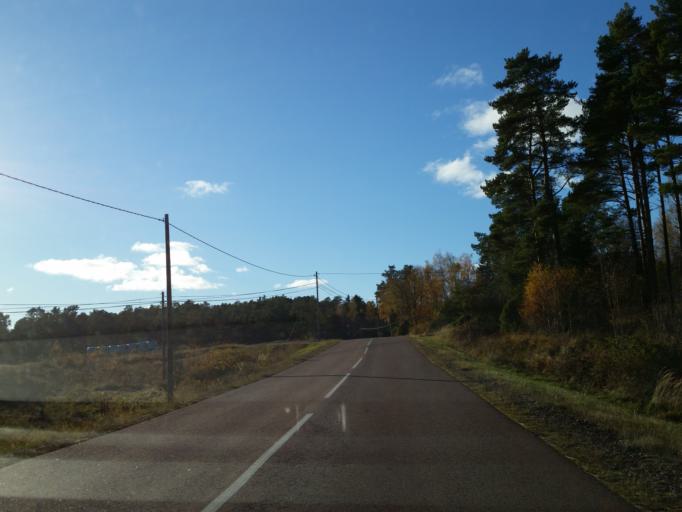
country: AX
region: Alands landsbygd
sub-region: Geta
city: Geta
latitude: 60.3700
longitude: 19.8036
